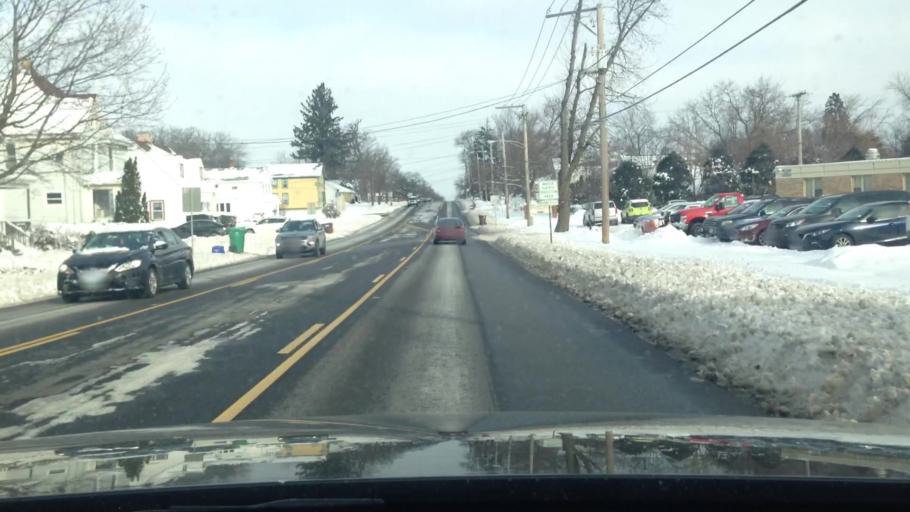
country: US
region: Illinois
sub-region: McHenry County
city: Woodstock
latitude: 42.3202
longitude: -88.4431
